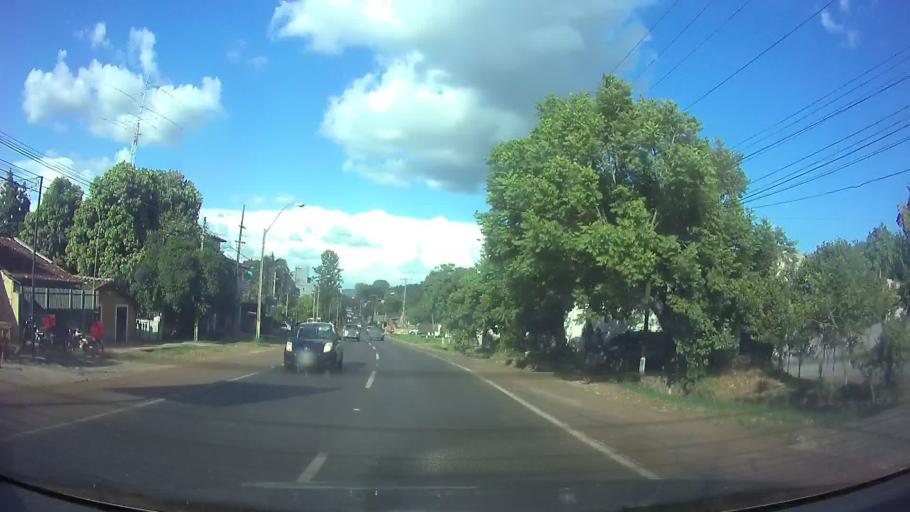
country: PY
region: Cordillera
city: Caacupe
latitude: -25.3885
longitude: -57.1477
